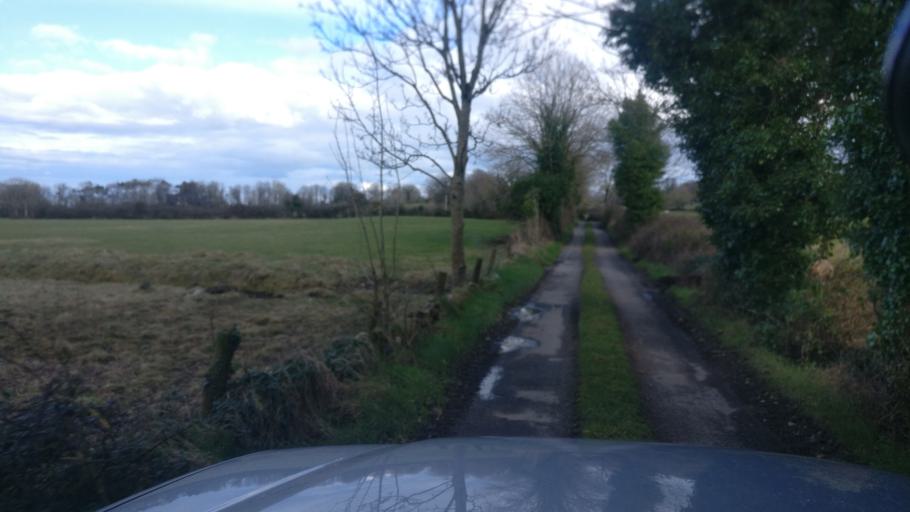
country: IE
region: Connaught
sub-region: County Galway
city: Loughrea
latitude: 53.1833
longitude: -8.4338
